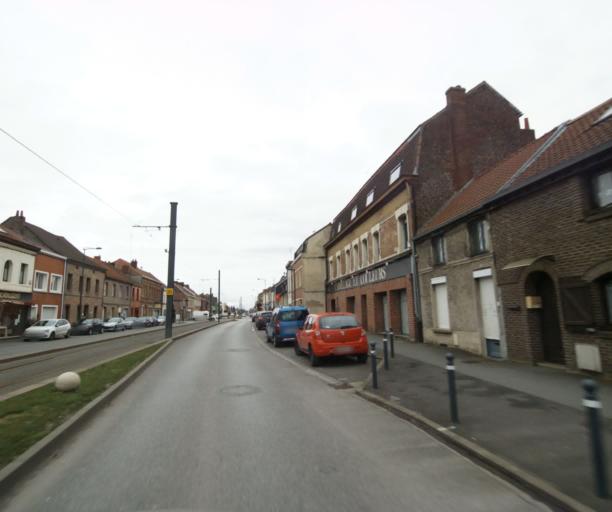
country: FR
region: Nord-Pas-de-Calais
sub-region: Departement du Nord
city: Bruay-sur-l'Escaut
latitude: 50.3962
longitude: 3.5378
